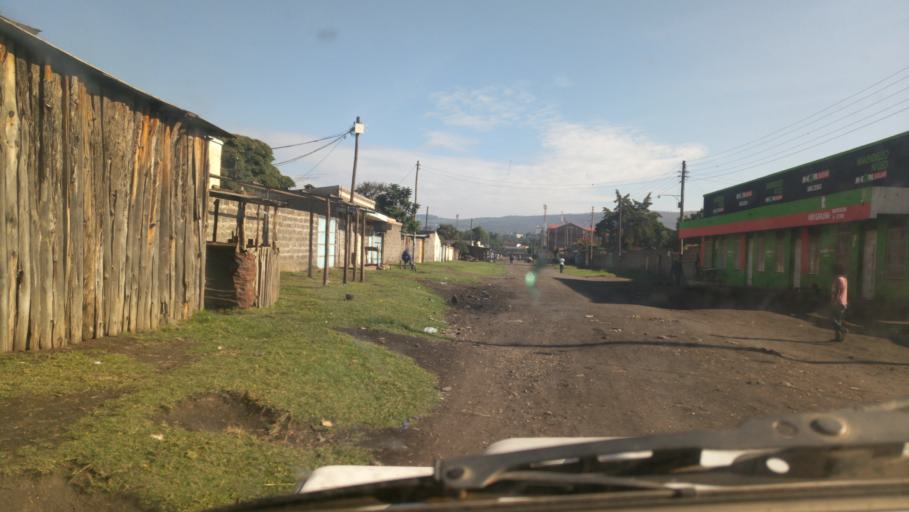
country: KE
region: Nakuru
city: Nakuru
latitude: -0.3002
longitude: 36.0761
